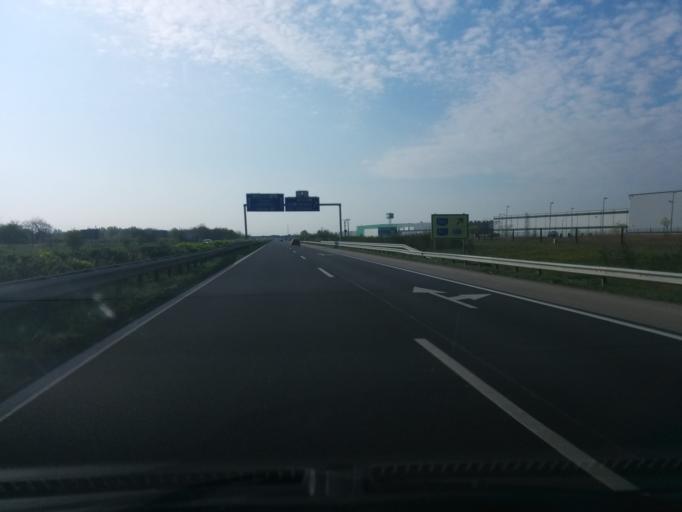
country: HU
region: Pest
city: Gyal
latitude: 47.3666
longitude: 19.1911
